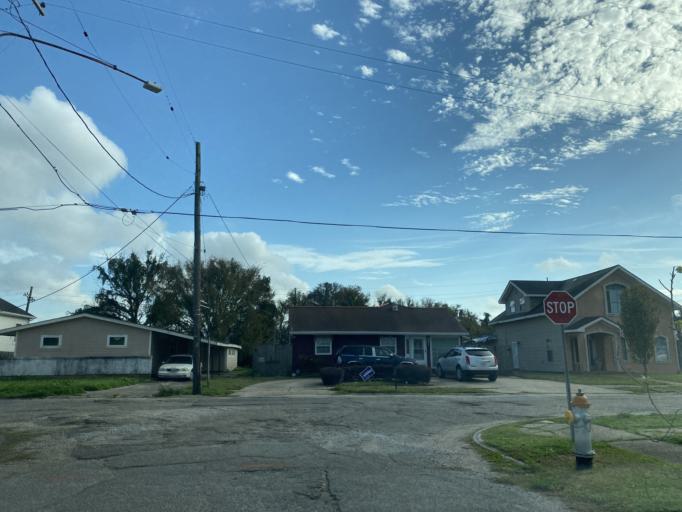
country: US
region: Louisiana
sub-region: Saint Bernard Parish
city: Arabi
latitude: 30.0243
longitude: -90.0378
